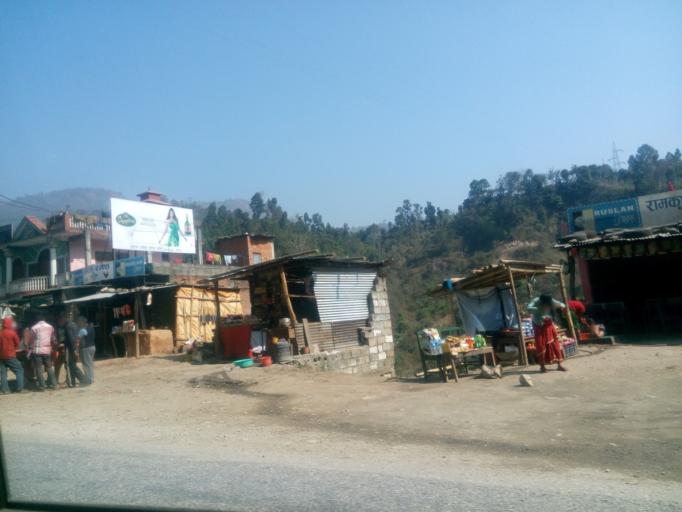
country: NP
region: Central Region
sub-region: Narayani Zone
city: Bharatpur
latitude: 27.8112
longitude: 84.8155
